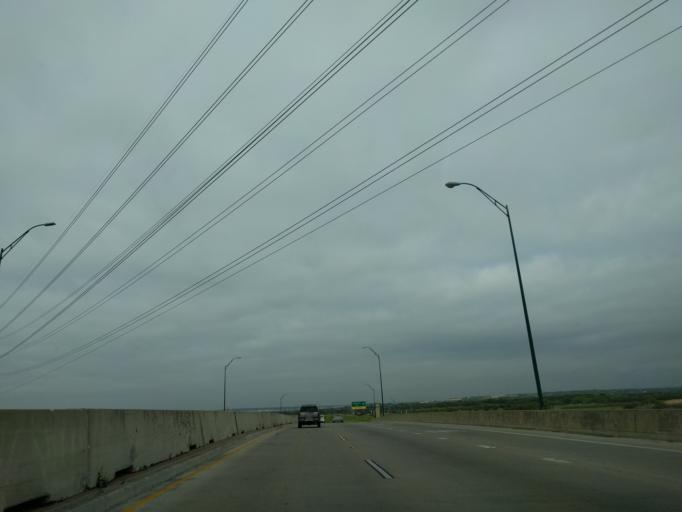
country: US
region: Texas
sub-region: Bexar County
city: Windcrest
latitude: 29.5462
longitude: -98.4356
